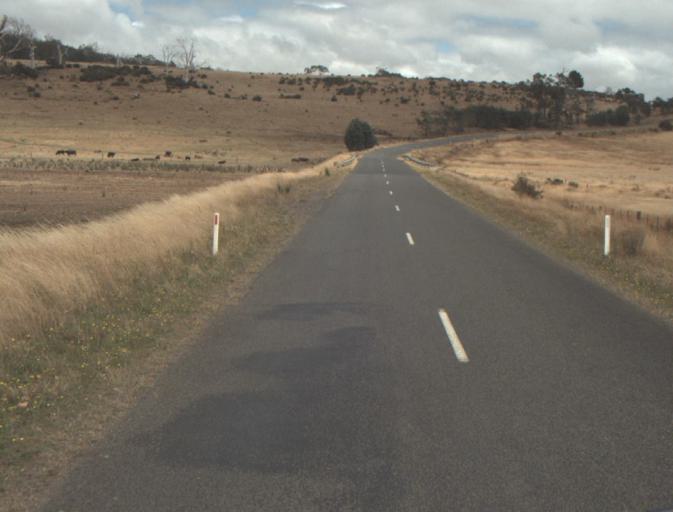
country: AU
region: Tasmania
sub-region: Northern Midlands
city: Evandale
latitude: -41.5069
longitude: 147.3731
